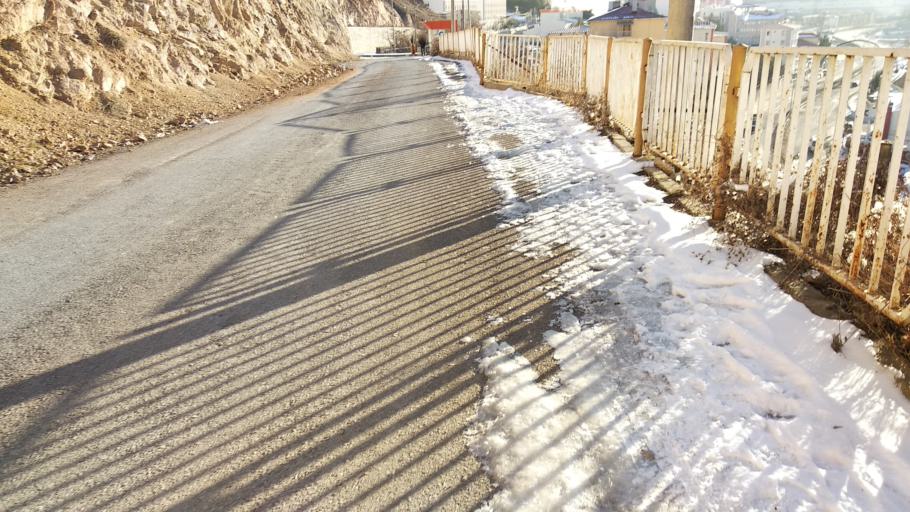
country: TR
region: Gumushane
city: Gumushkhane
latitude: 40.4372
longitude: 39.5109
